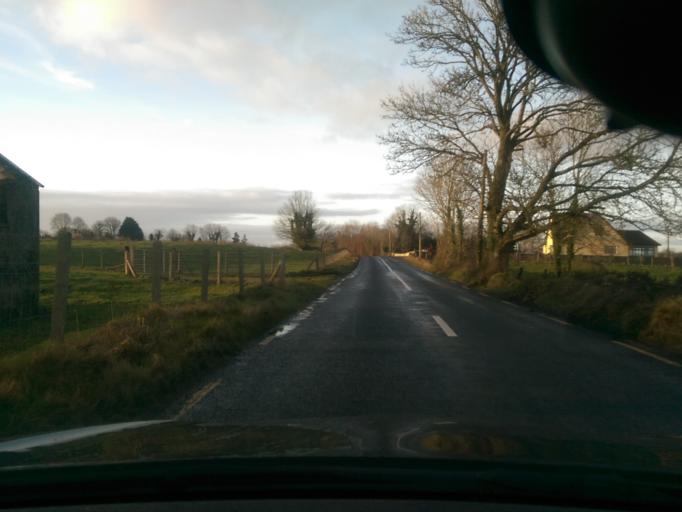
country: IE
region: Connaught
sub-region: County Galway
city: Athenry
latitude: 53.4001
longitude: -8.6499
